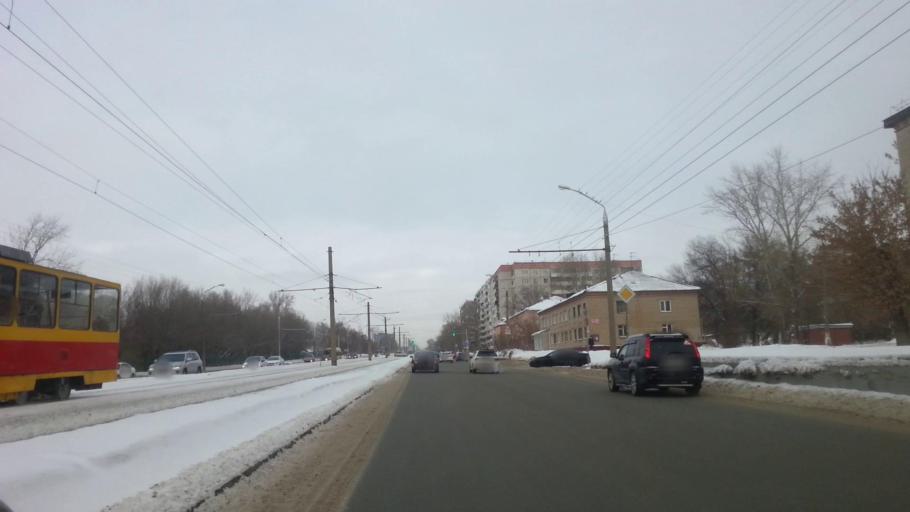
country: RU
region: Altai Krai
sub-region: Gorod Barnaulskiy
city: Barnaul
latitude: 53.3746
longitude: 83.7132
